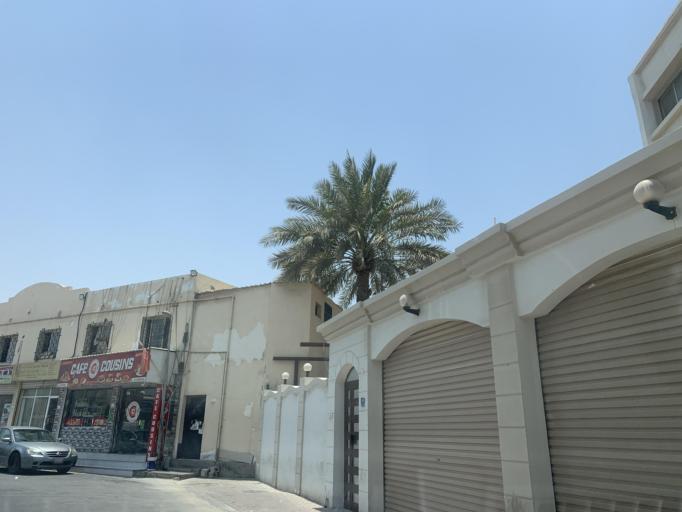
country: BH
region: Manama
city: Jidd Hafs
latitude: 26.2168
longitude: 50.5639
